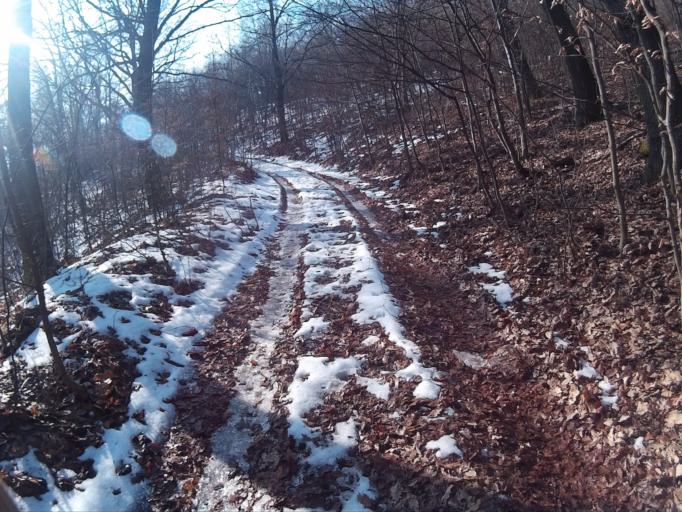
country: HU
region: Nograd
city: Paszto
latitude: 47.9833
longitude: 19.6782
